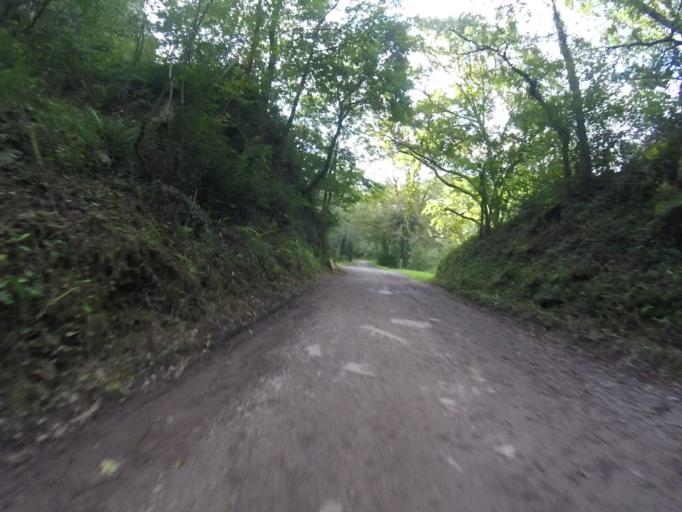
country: ES
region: Basque Country
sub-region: Provincia de Guipuzcoa
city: Andoain
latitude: 43.1891
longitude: -2.0052
